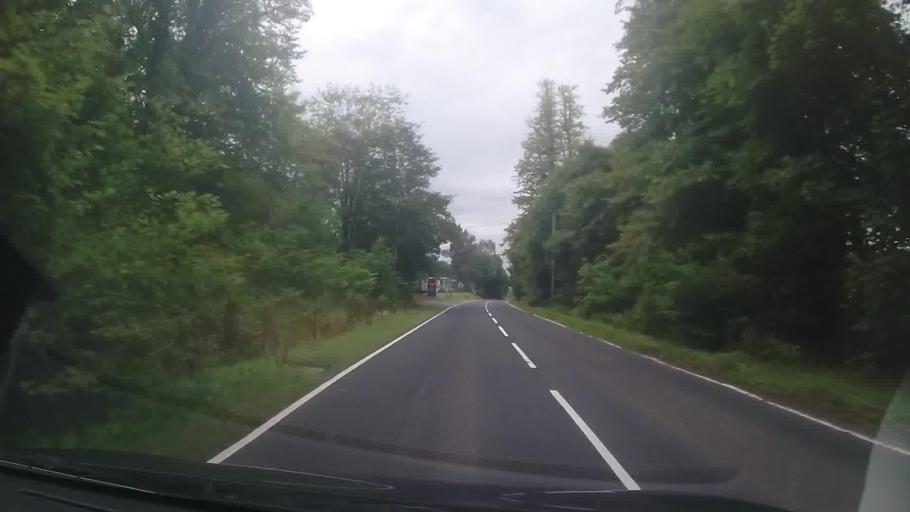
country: GB
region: Scotland
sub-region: Argyll and Bute
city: Garelochhead
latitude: 56.2249
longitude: -5.0255
